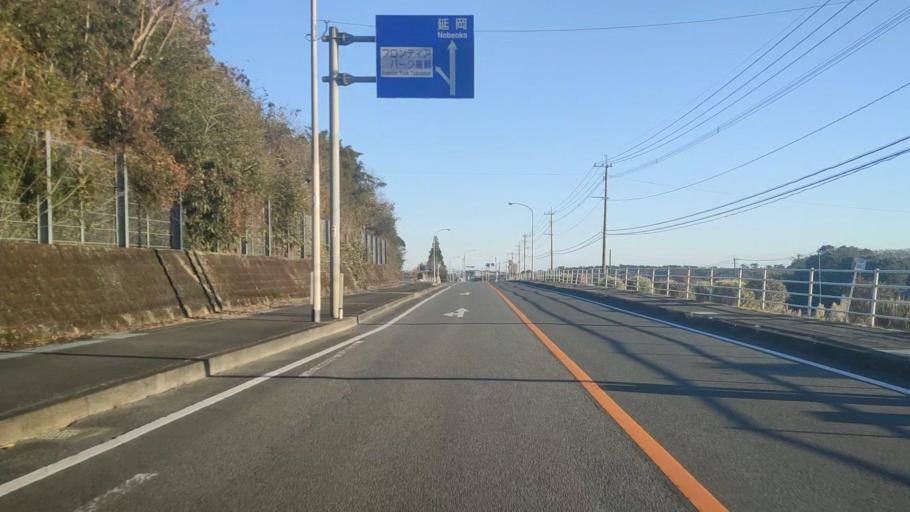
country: JP
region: Miyazaki
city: Takanabe
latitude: 32.1121
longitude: 131.5272
